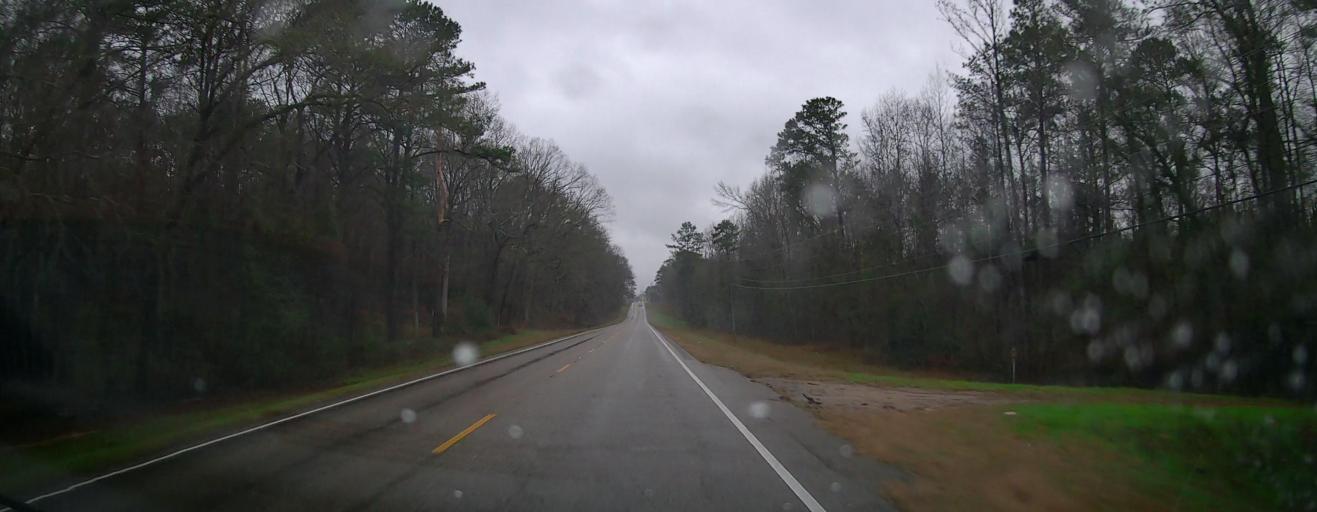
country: US
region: Alabama
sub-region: Autauga County
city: Prattville
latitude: 32.4853
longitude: -86.5375
